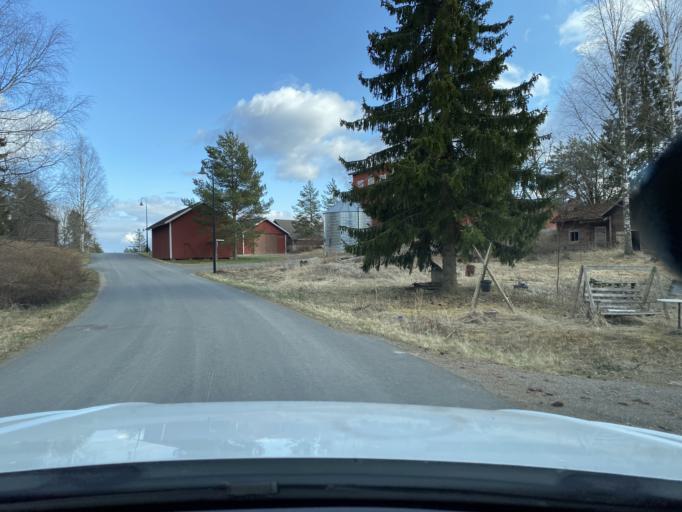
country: FI
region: Pirkanmaa
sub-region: Lounais-Pirkanmaa
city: Punkalaidun
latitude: 61.1202
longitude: 23.0778
